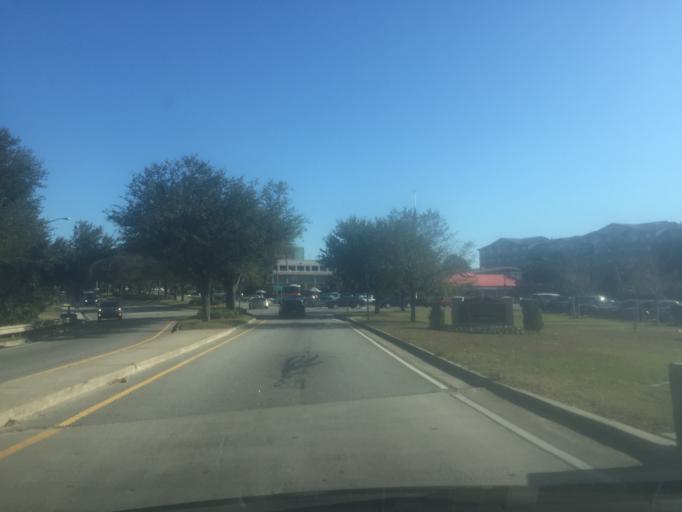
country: US
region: Georgia
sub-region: Chatham County
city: Savannah
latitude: 32.0800
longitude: -81.1031
